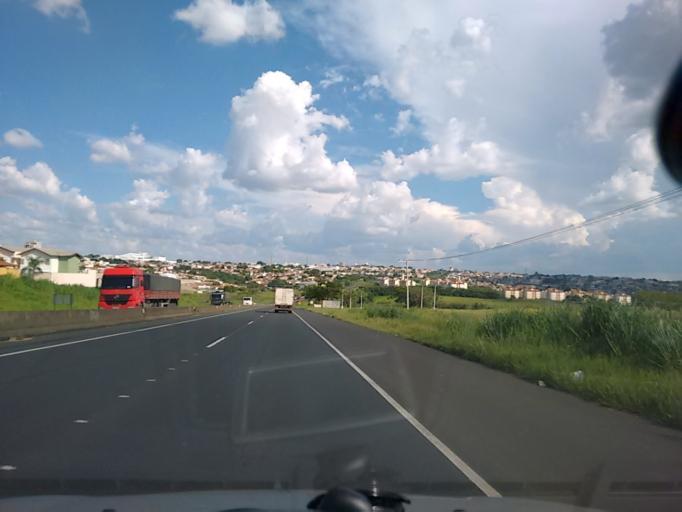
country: BR
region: Sao Paulo
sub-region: Marilia
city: Marilia
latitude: -22.1869
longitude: -49.9695
